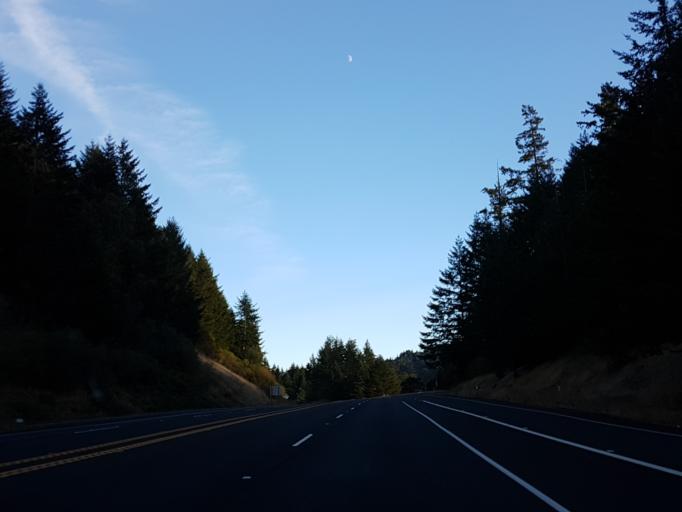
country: US
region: California
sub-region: Humboldt County
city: Redway
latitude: 39.9422
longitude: -123.7786
